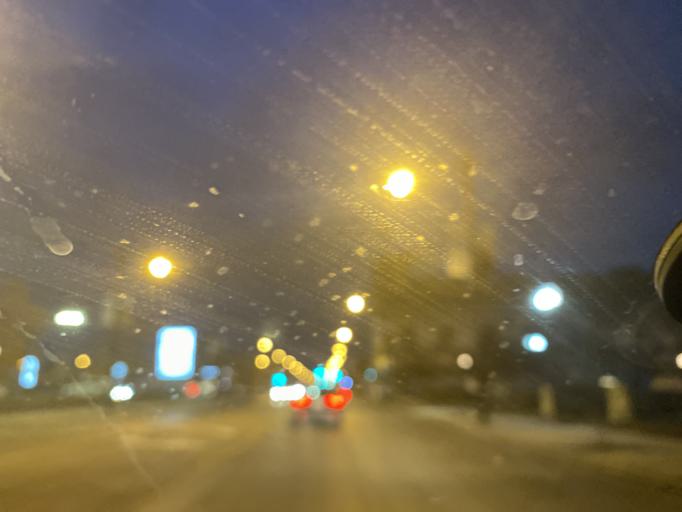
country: US
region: Illinois
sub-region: Cook County
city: Chicago
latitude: 41.7797
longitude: -87.6467
